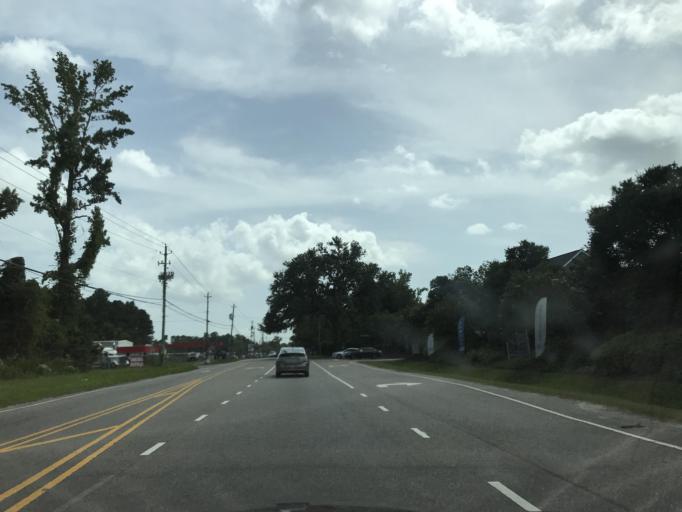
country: US
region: North Carolina
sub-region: New Hanover County
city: Wrightsboro
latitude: 34.2774
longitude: -77.9247
